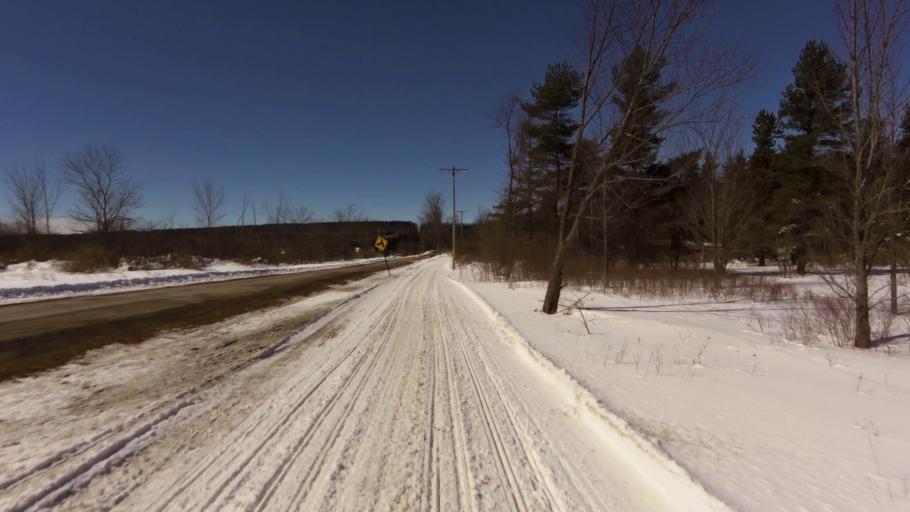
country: US
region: New York
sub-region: Allegany County
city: Houghton
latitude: 42.4115
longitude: -78.2966
